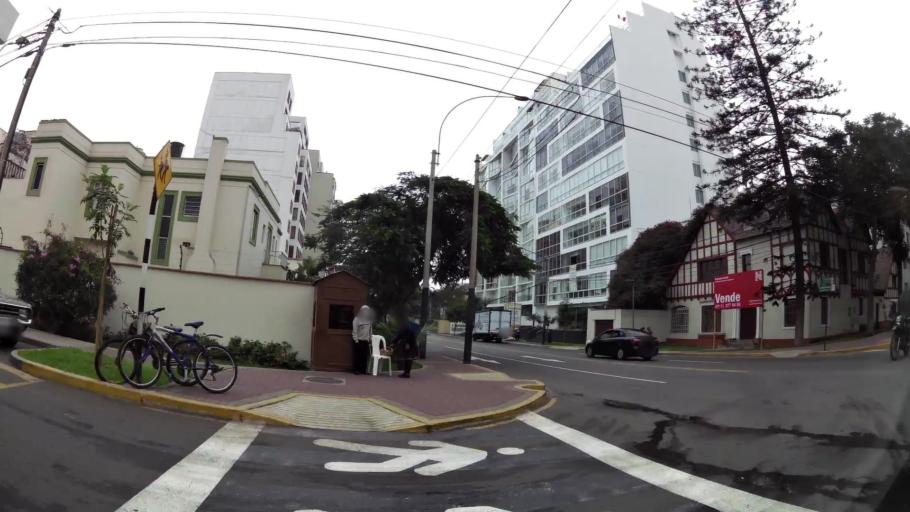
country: PE
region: Lima
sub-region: Lima
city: San Isidro
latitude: -12.0958
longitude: -77.0436
